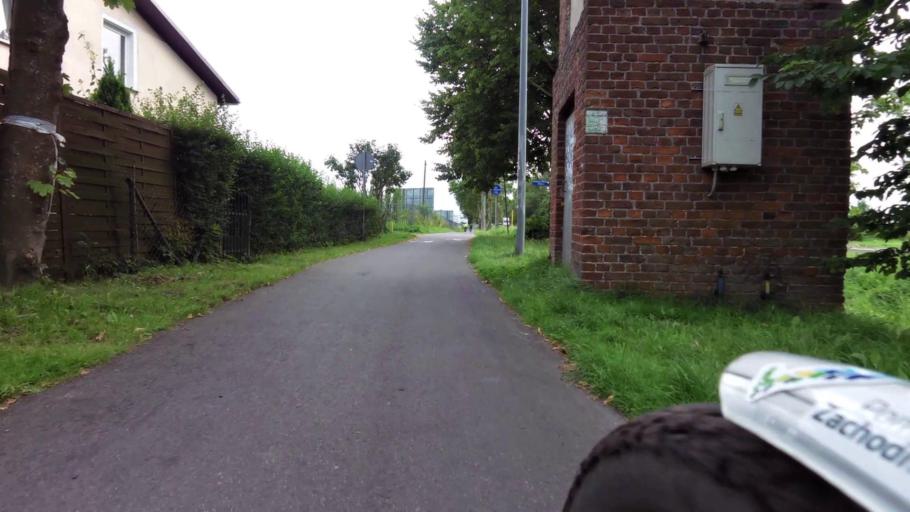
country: PL
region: West Pomeranian Voivodeship
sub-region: Powiat koszalinski
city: Mielno
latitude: 54.2494
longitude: 16.0610
